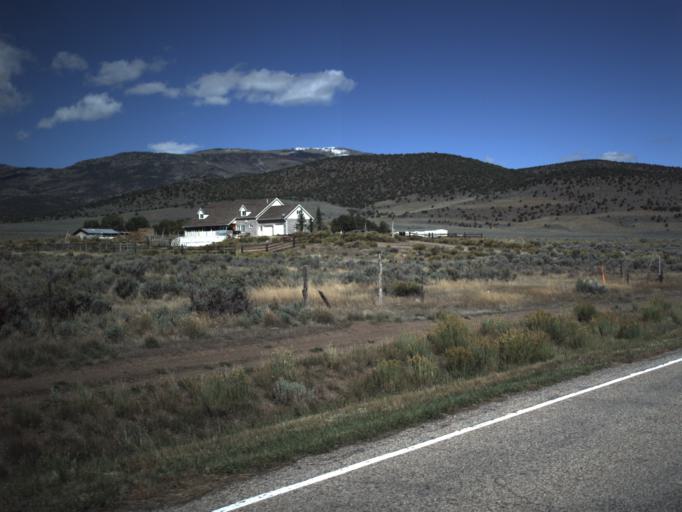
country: US
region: Utah
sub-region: Sevier County
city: Monroe
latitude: 38.5177
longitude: -111.8814
